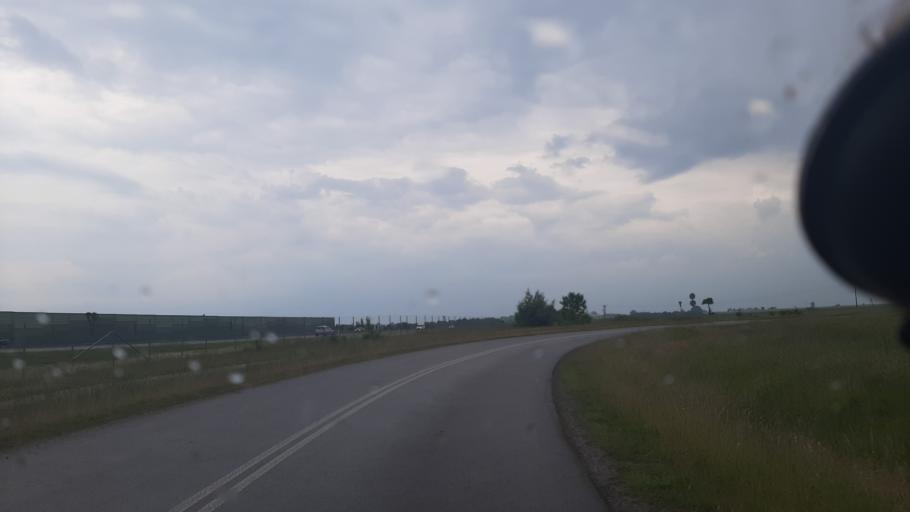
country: PL
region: Lublin Voivodeship
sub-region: Powiat lubelski
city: Garbow
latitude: 51.3503
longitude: 22.3681
